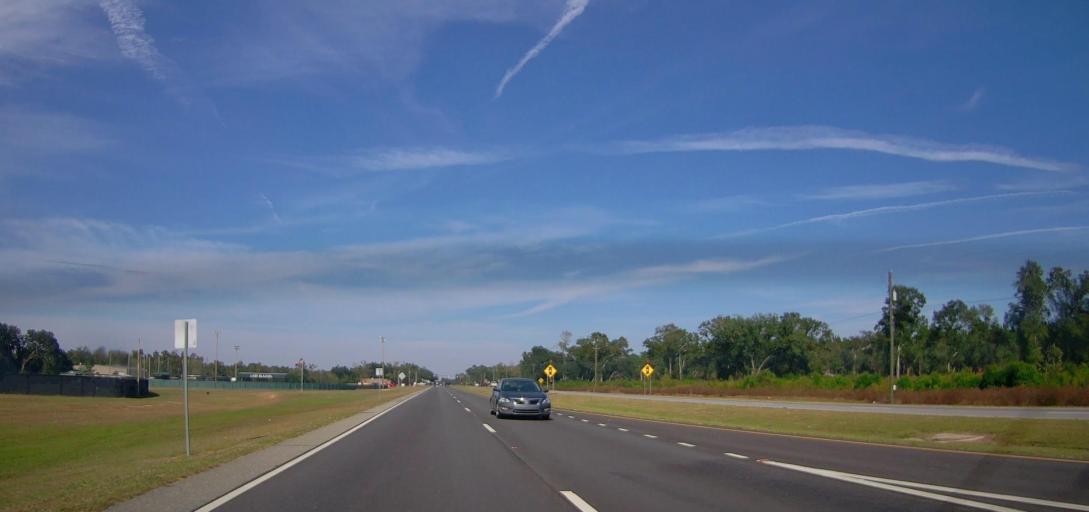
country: US
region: Georgia
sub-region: Dougherty County
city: Putney
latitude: 31.3756
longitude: -84.1514
